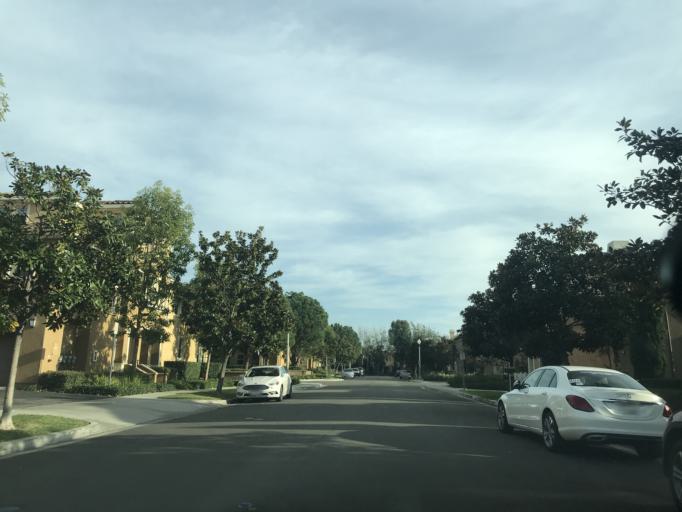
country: US
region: California
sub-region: Orange County
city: North Tustin
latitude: 33.6999
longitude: -117.7495
